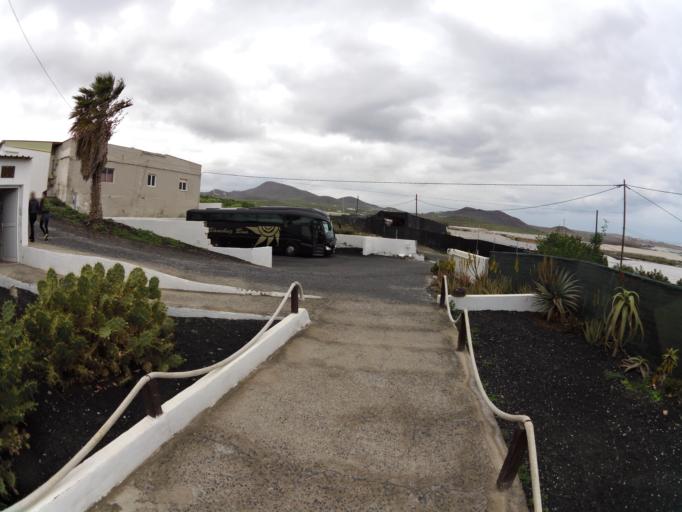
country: ES
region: Canary Islands
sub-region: Provincia de Las Palmas
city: Ingenio
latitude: 27.9297
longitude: -15.4146
